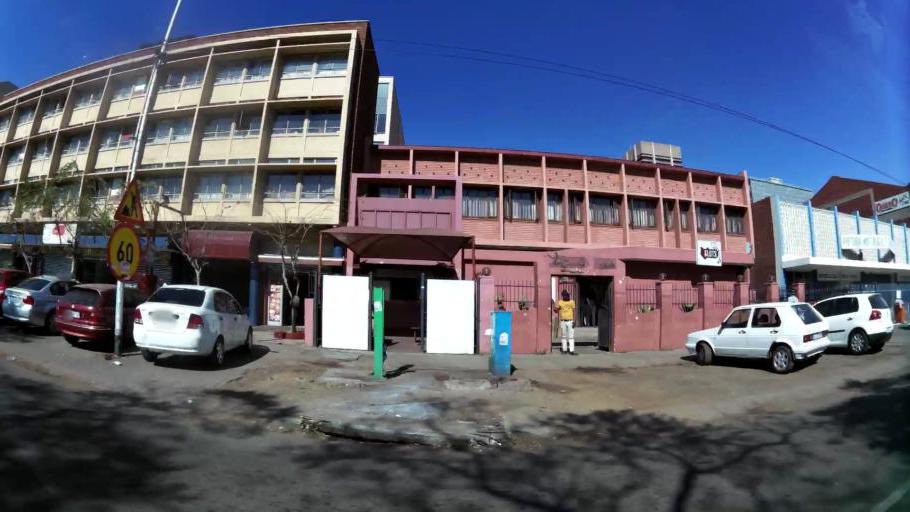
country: ZA
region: Gauteng
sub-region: City of Tshwane Metropolitan Municipality
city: Pretoria
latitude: -25.7418
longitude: 28.1915
